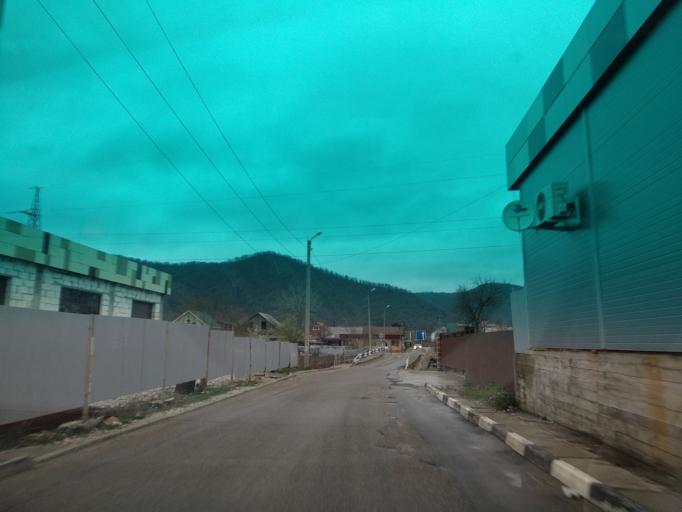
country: RU
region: Krasnodarskiy
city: Novomikhaylovskiy
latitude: 44.2589
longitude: 38.8618
